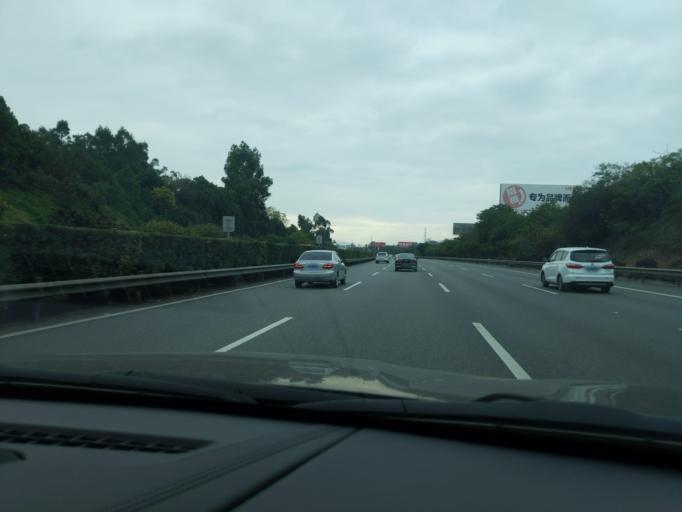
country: CN
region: Fujian
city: Neikeng
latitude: 24.7739
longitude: 118.4559
